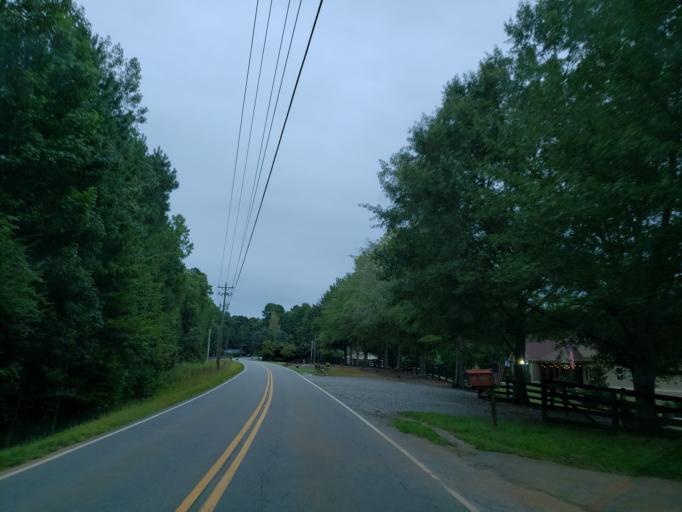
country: US
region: Georgia
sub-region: Cherokee County
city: Canton
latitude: 34.3381
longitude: -84.4905
